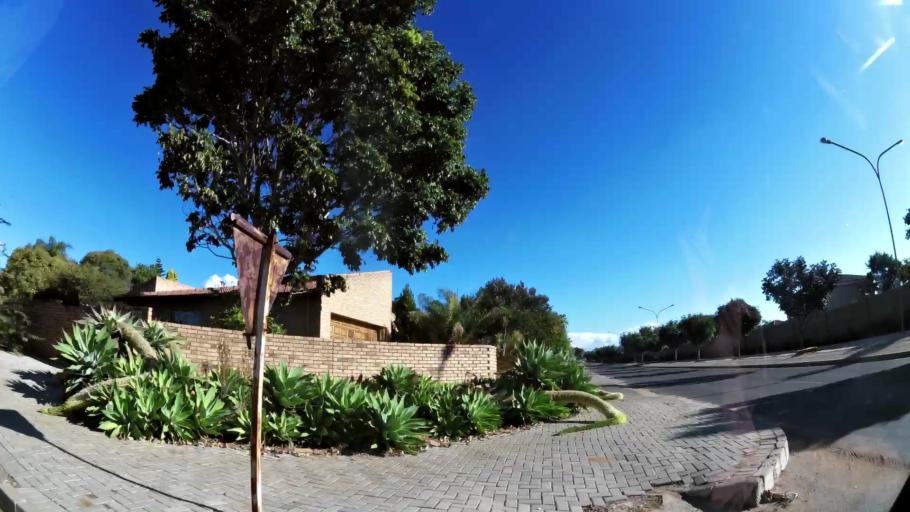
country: ZA
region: Limpopo
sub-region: Capricorn District Municipality
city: Polokwane
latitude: -23.8790
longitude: 29.4920
